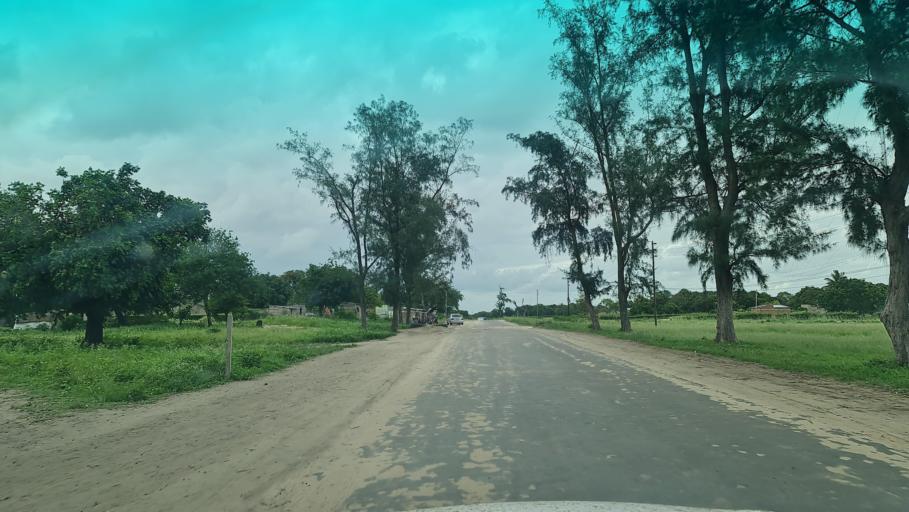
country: MZ
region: Maputo
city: Manhica
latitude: -25.4466
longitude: 32.7753
